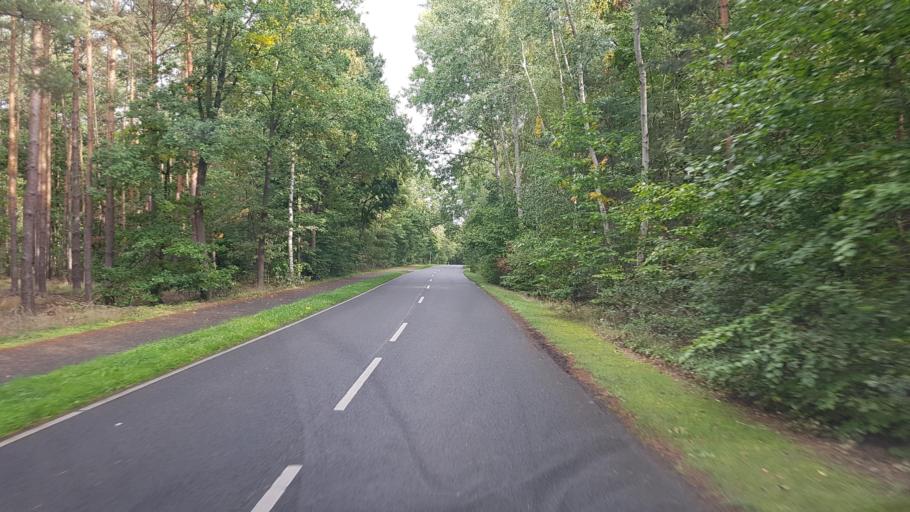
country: DE
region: Brandenburg
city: Doberlug-Kirchhain
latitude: 51.6311
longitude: 13.5282
